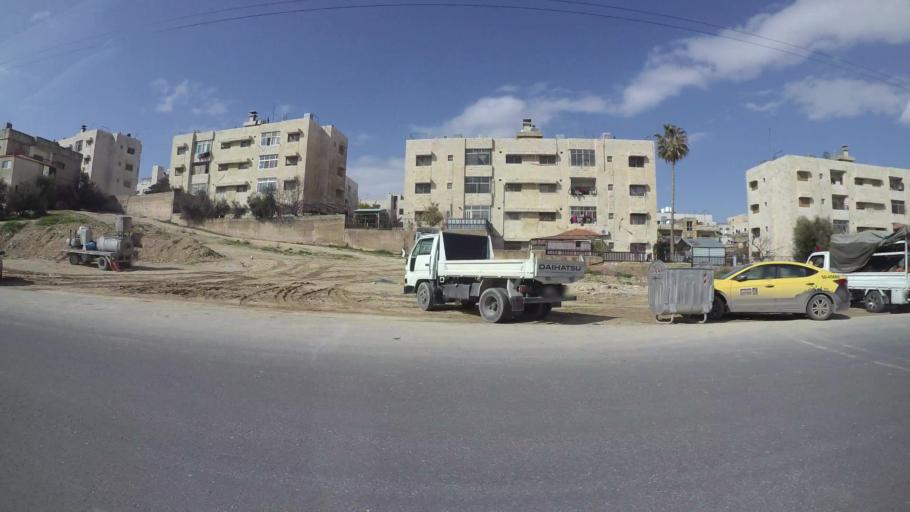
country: JO
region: Amman
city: Al Jubayhah
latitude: 32.0176
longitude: 35.8502
